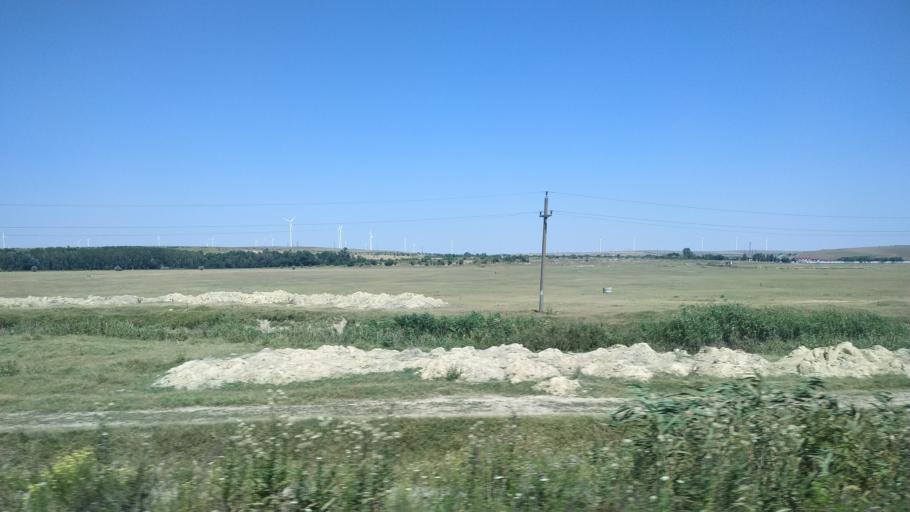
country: RO
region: Constanta
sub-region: Comuna Mircea Voda
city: Mircea Voda
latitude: 44.2642
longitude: 28.1655
